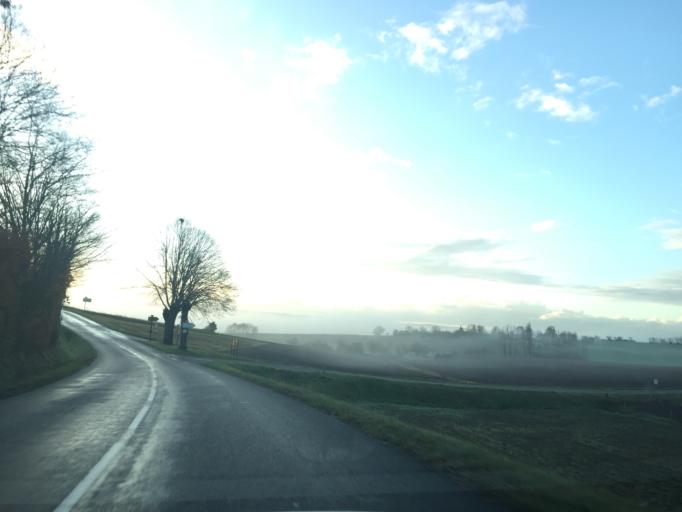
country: FR
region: Aquitaine
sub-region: Departement de la Dordogne
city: Saint-Aulaye
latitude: 45.2677
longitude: 0.1681
